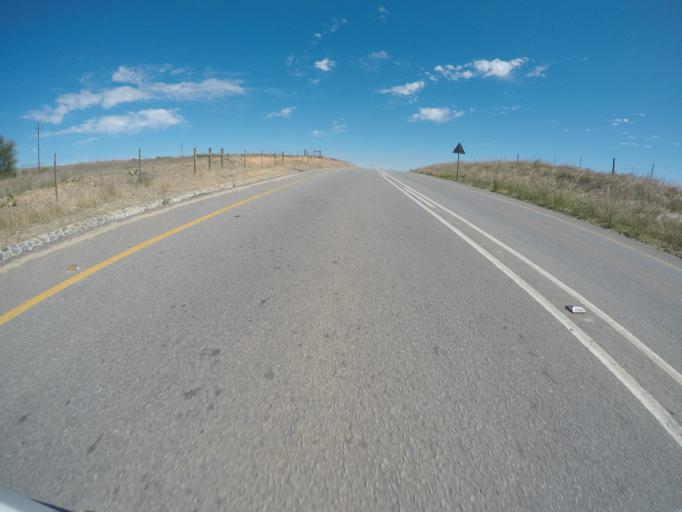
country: ZA
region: Western Cape
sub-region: West Coast District Municipality
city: Malmesbury
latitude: -33.4792
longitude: 18.7118
